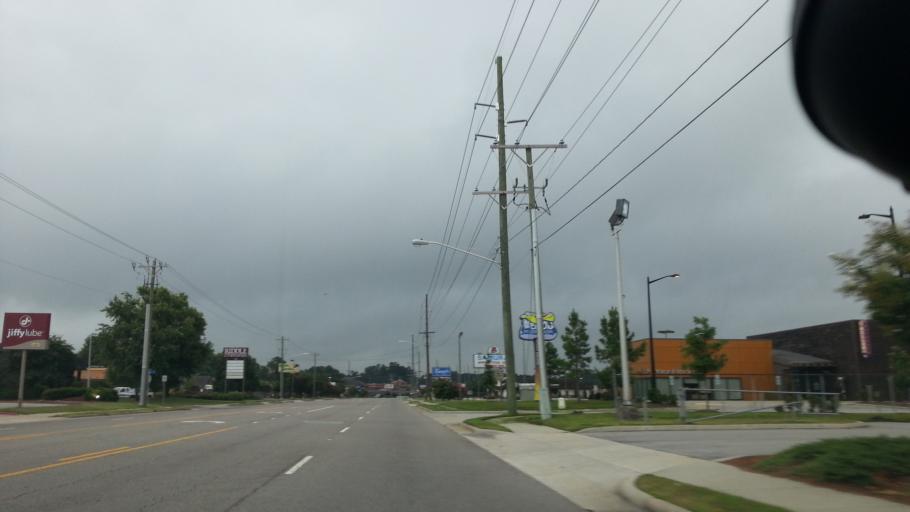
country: US
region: North Carolina
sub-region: Cumberland County
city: Fayetteville
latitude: 35.0726
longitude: -78.9526
